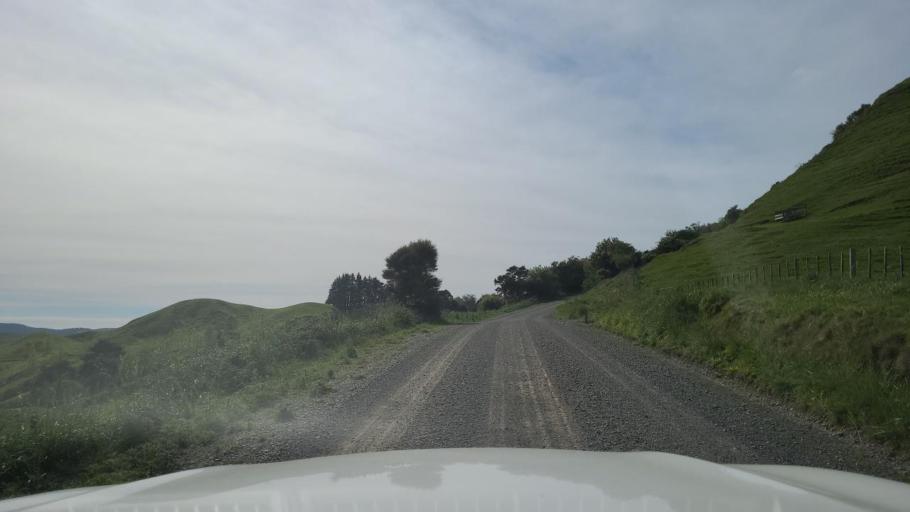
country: NZ
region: Hawke's Bay
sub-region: Napier City
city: Taradale
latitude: -39.3387
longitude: 176.6628
